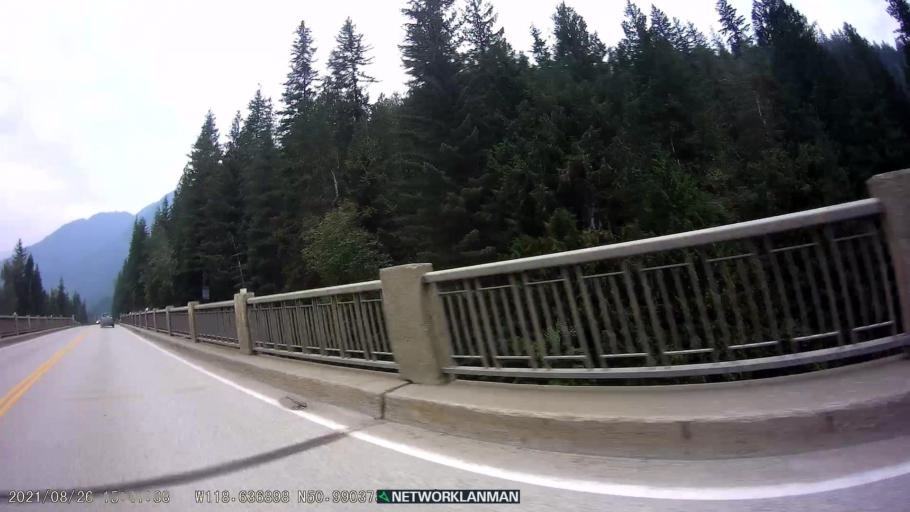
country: CA
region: British Columbia
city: Sicamous
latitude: 50.9903
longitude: -118.6368
